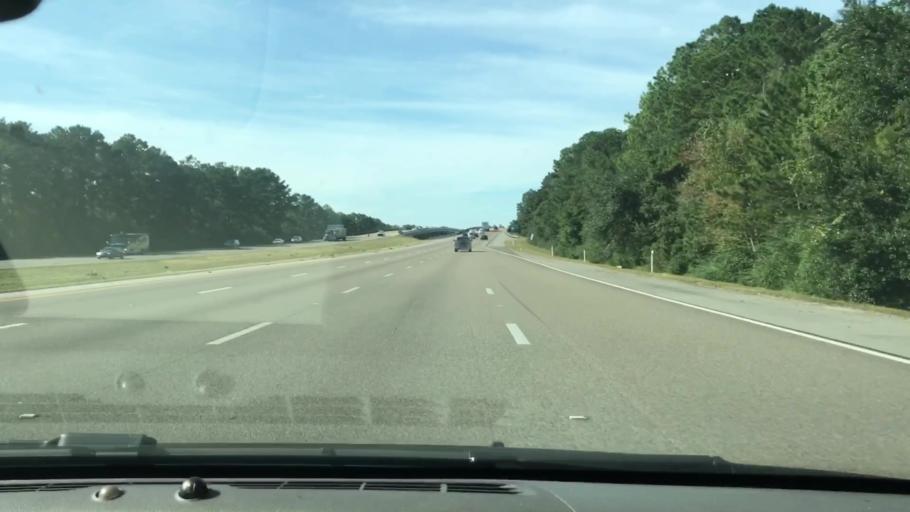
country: US
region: Mississippi
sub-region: Harrison County
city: D'Iberville
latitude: 30.4516
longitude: -88.9388
